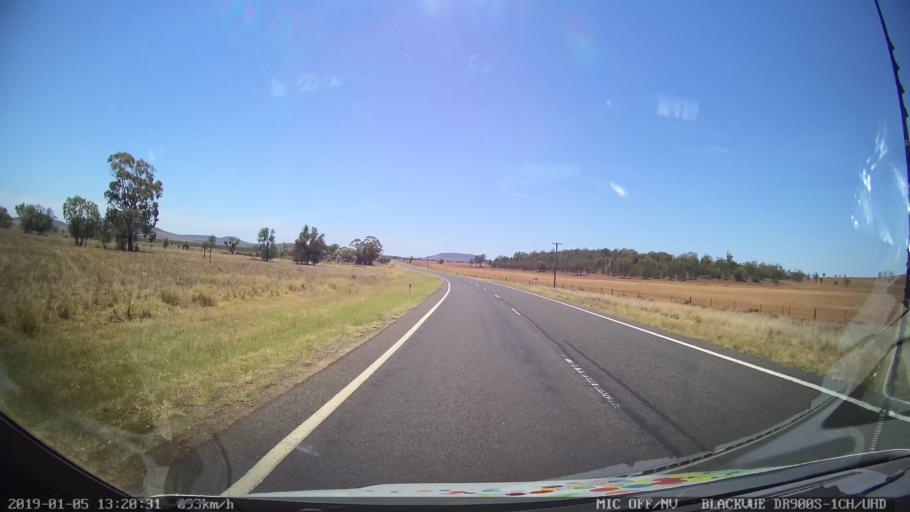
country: AU
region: New South Wales
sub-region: Gunnedah
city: Gunnedah
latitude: -31.1017
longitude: 149.9365
